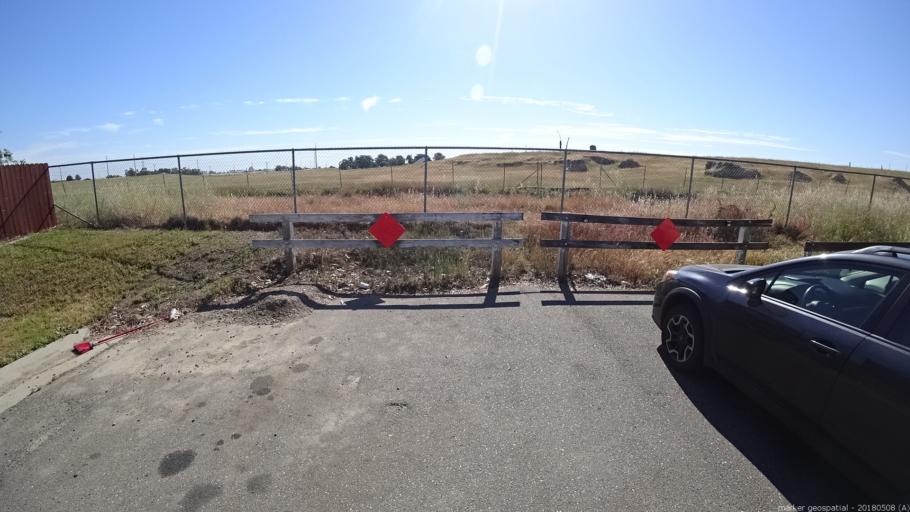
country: US
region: California
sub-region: Sacramento County
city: Elverta
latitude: 38.6827
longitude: -121.4937
